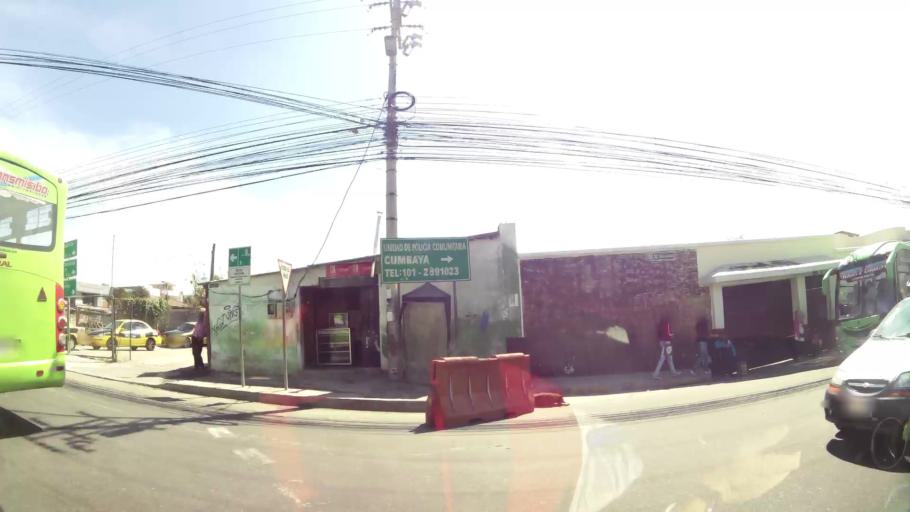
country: EC
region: Pichincha
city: Quito
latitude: -0.2024
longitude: -78.4299
